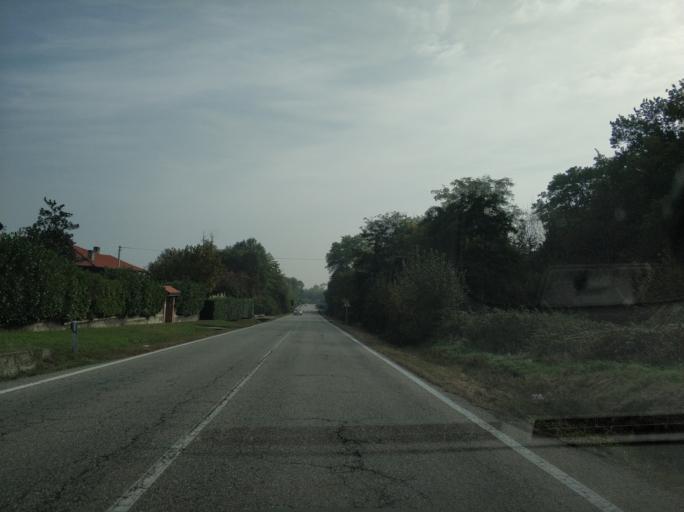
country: IT
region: Piedmont
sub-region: Provincia di Biella
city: Ceresane-Curanuova
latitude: 45.5131
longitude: 7.9972
